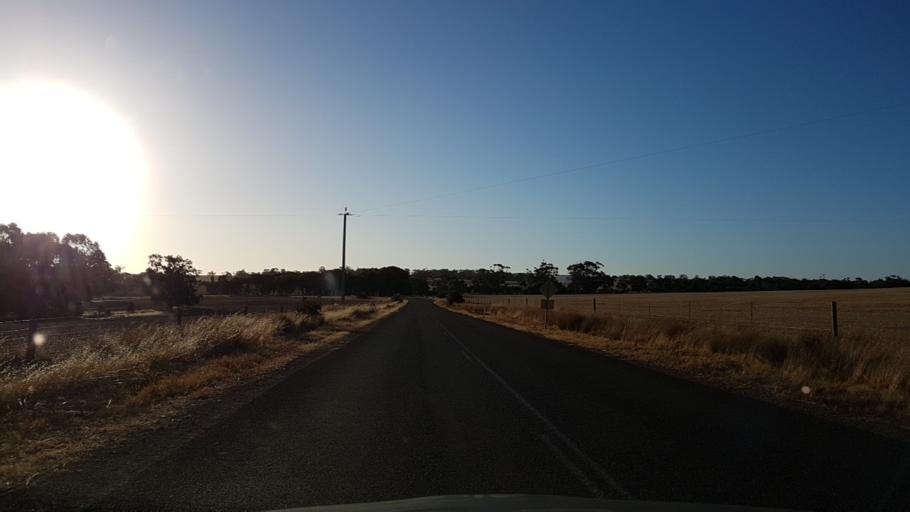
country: AU
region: South Australia
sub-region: Clare and Gilbert Valleys
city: Clare
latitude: -33.9990
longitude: 138.7447
